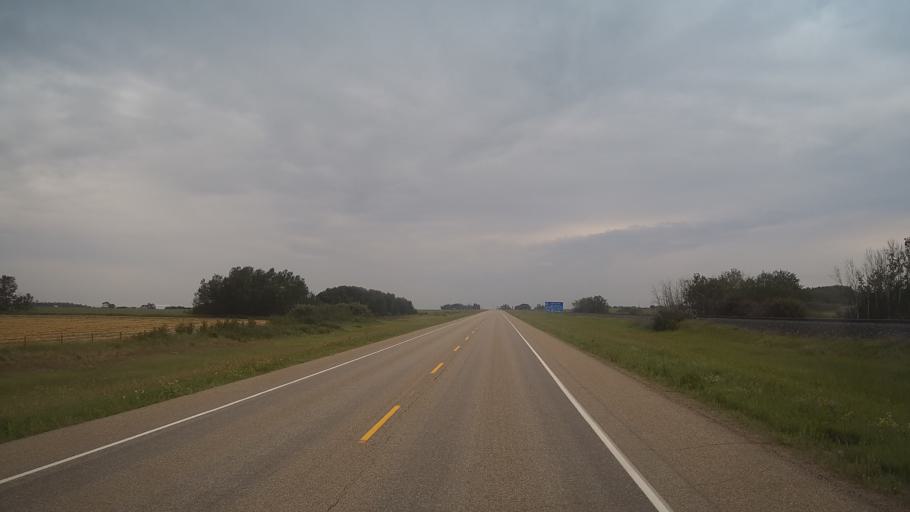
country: CA
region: Saskatchewan
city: Langham
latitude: 52.1267
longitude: -107.2743
